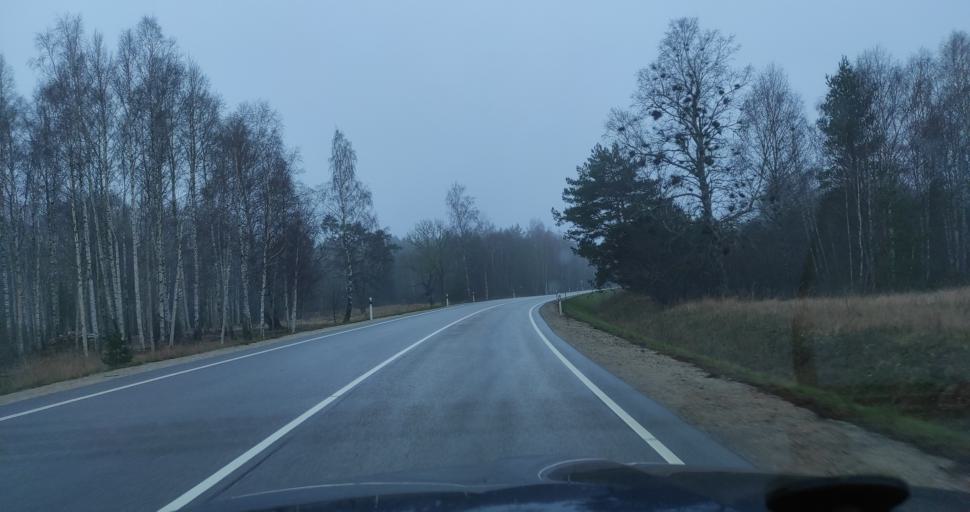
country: LV
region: Pavilostas
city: Pavilosta
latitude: 56.9239
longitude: 21.2652
